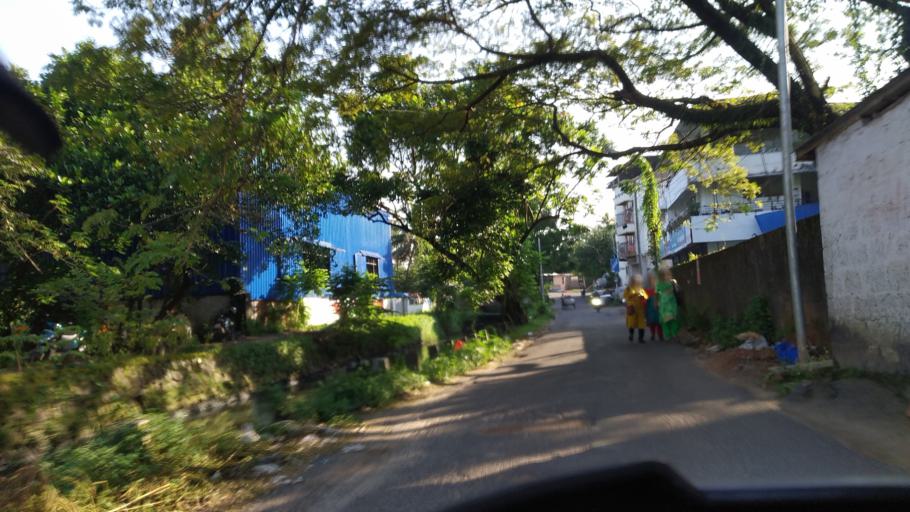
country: IN
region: Kerala
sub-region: Ernakulam
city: Cochin
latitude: 9.9842
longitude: 76.2913
